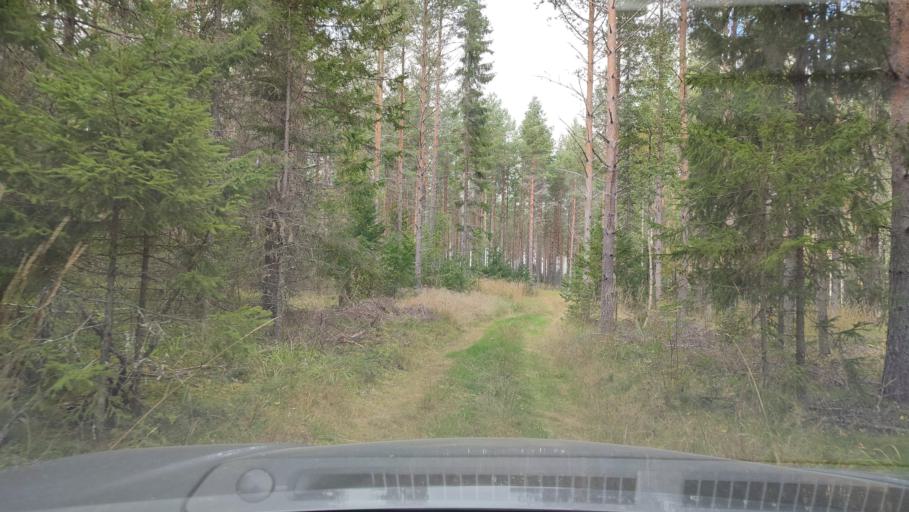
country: FI
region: Southern Ostrobothnia
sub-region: Suupohja
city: Karijoki
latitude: 62.2219
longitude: 21.6184
